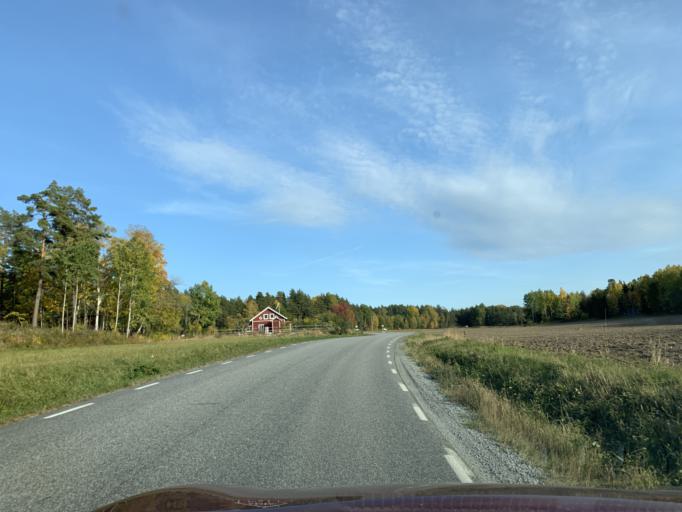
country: SE
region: Stockholm
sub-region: Upplands-Bro Kommun
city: Bro
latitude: 59.5083
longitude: 17.5962
